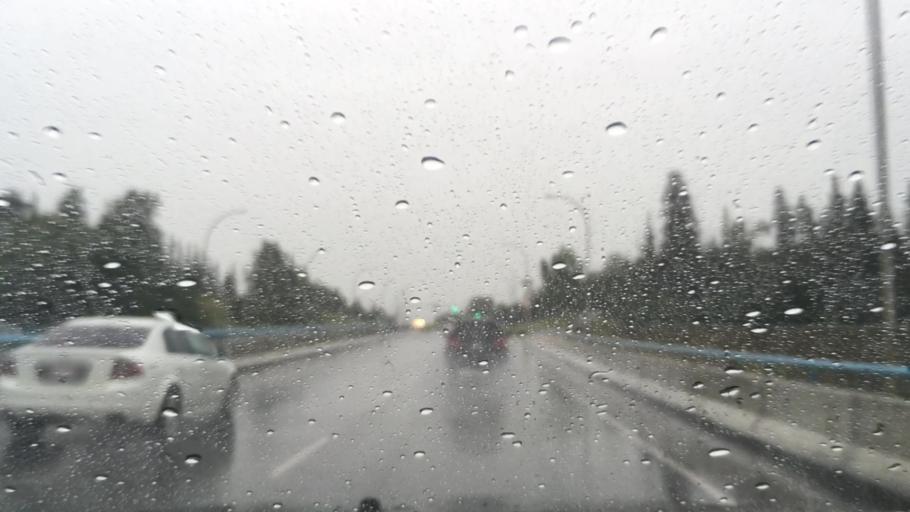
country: CA
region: Alberta
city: Edmonton
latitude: 53.4455
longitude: -113.5171
